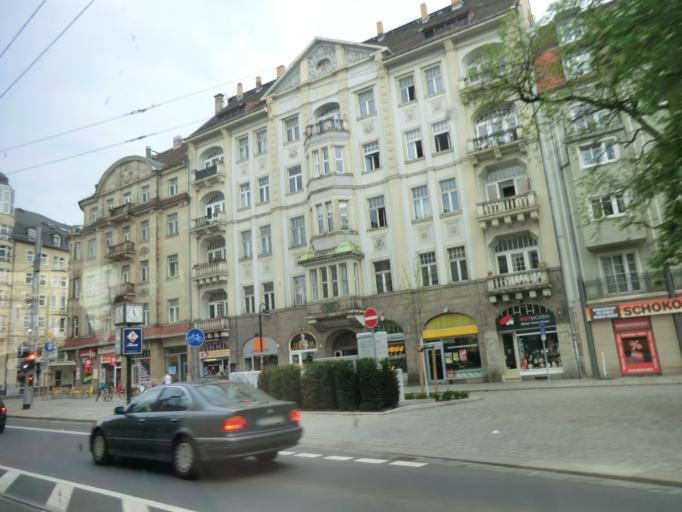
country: DE
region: Saxony
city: Dresden
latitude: 51.0629
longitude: 13.7513
